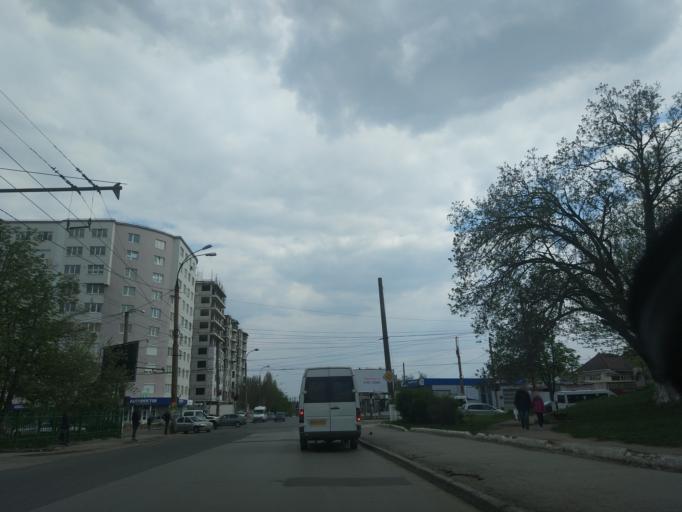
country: MD
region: Chisinau
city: Chisinau
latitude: 46.9835
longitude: 28.8777
